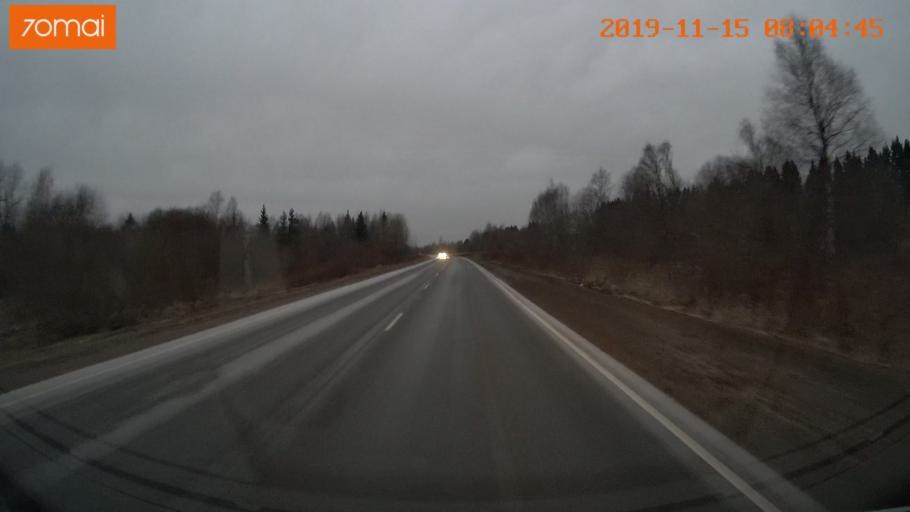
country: RU
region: Vologda
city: Cherepovets
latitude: 59.0112
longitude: 38.0707
